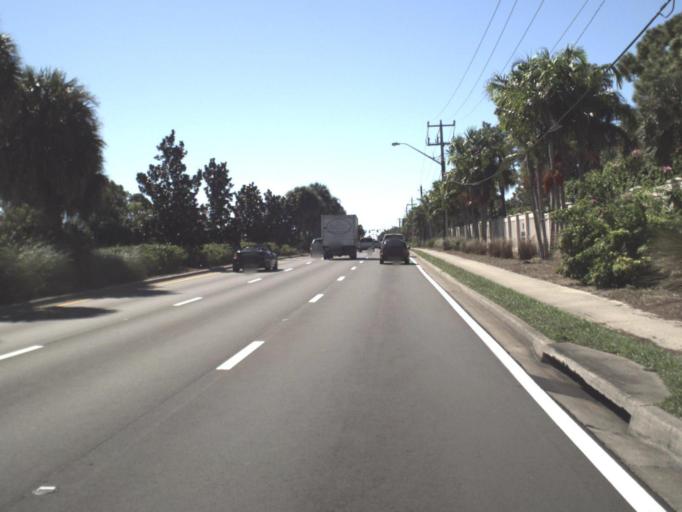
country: US
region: Florida
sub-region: Collier County
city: Naples
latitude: 26.1712
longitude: -81.7672
